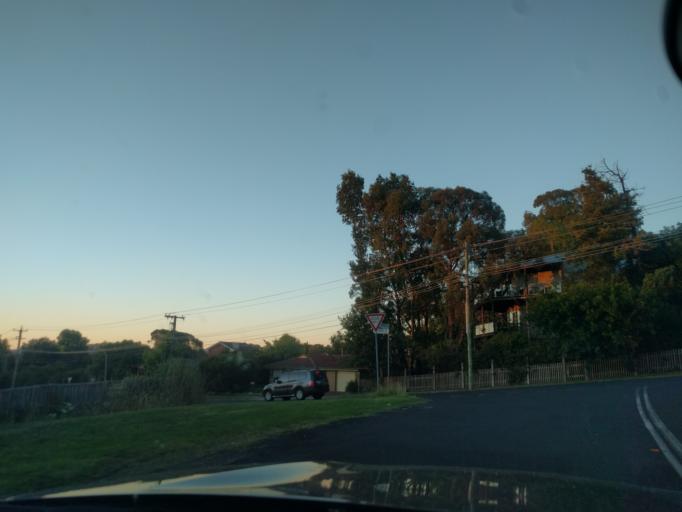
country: AU
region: New South Wales
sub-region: Armidale Dumaresq
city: Armidale
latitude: -30.5001
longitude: 151.6618
